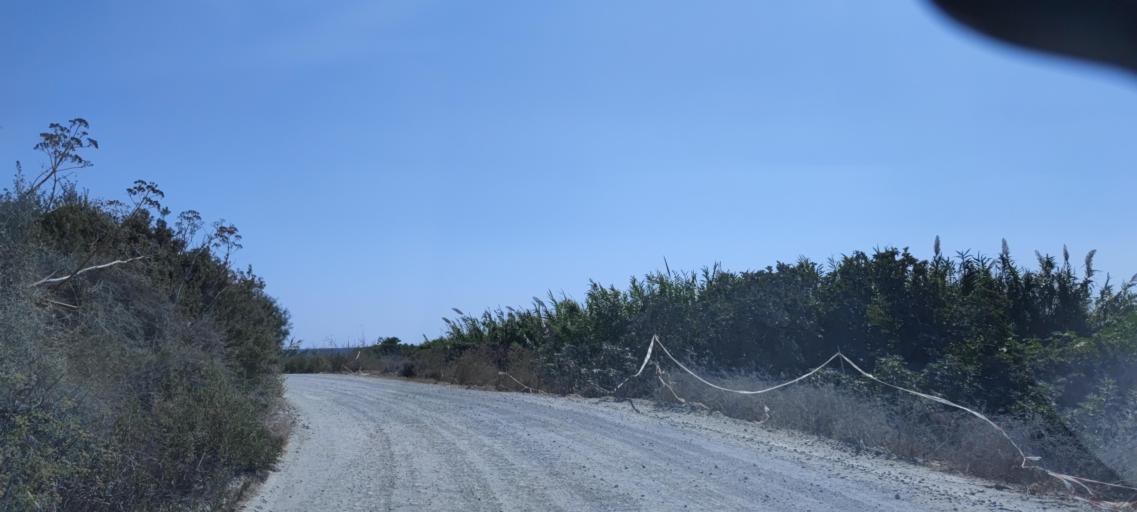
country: CY
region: Larnaka
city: Kofinou
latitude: 34.7764
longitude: 33.4684
